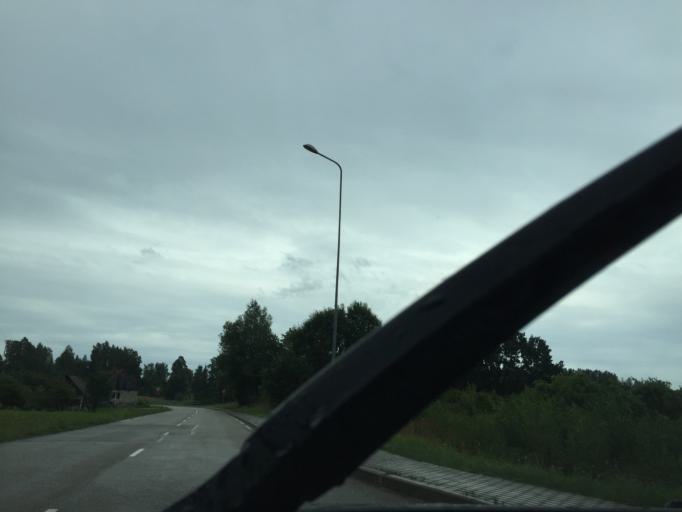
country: LV
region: Preilu Rajons
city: Jaunaglona
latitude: 56.2406
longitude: 27.2165
